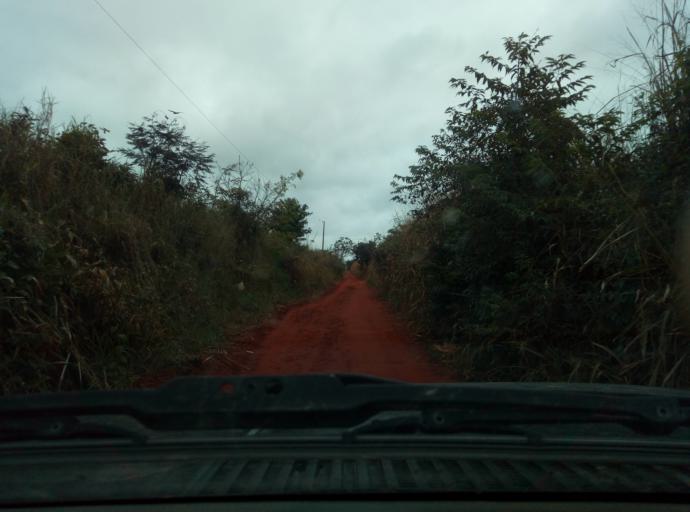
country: PY
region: Caaguazu
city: Doctor Cecilio Baez
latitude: -25.1587
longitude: -56.2717
